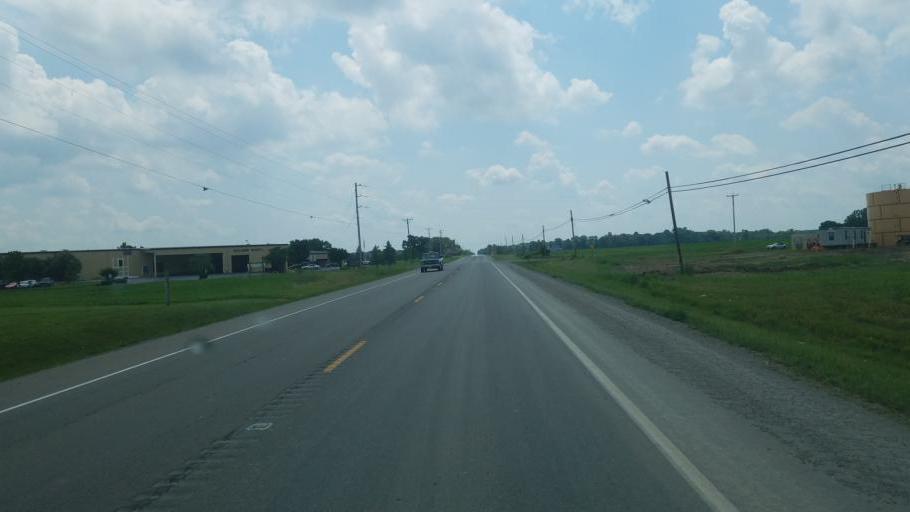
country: US
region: Ohio
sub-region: Hardin County
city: Kenton
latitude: 40.6140
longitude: -83.6270
